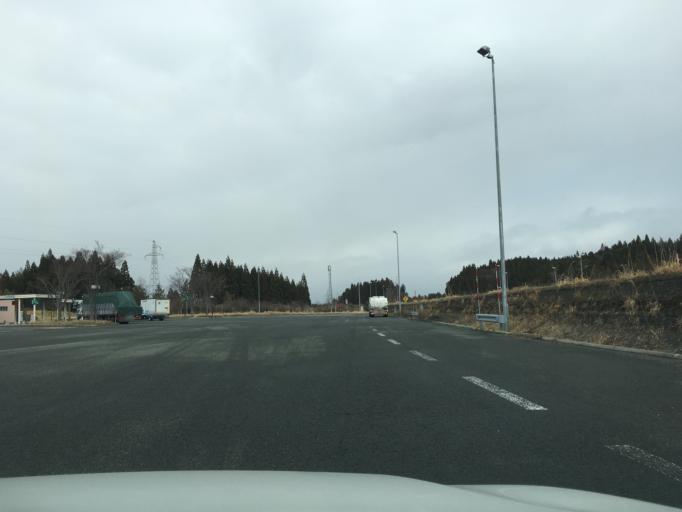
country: JP
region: Akita
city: Tenno
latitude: 40.0088
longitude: 140.0871
